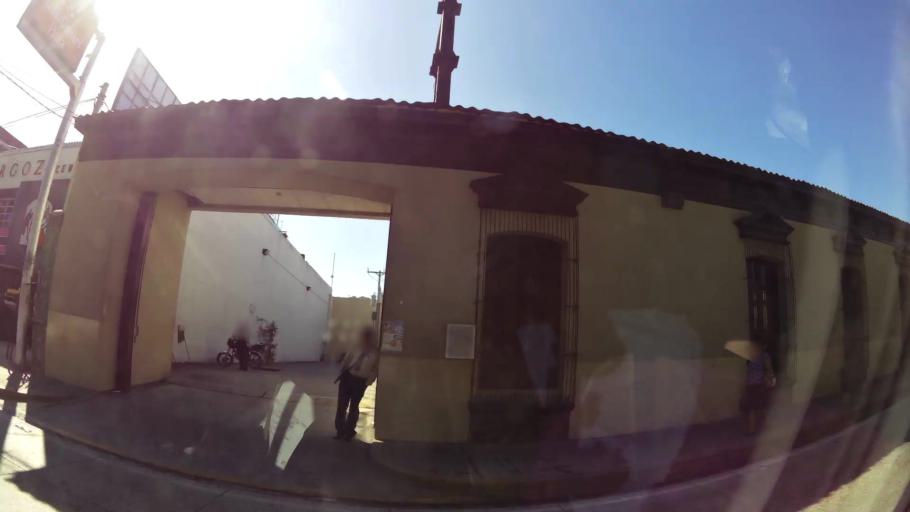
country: SV
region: La Libertad
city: Santa Tecla
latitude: 13.6731
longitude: -89.2855
